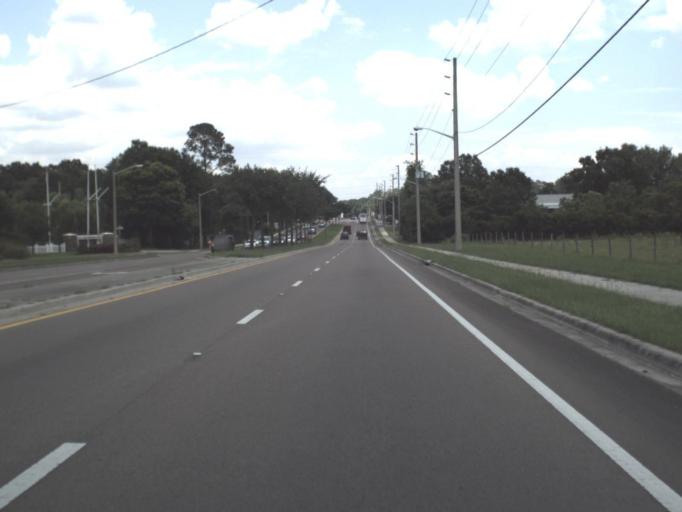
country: US
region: Florida
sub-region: Alachua County
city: Newberry
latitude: 29.6539
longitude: -82.5006
